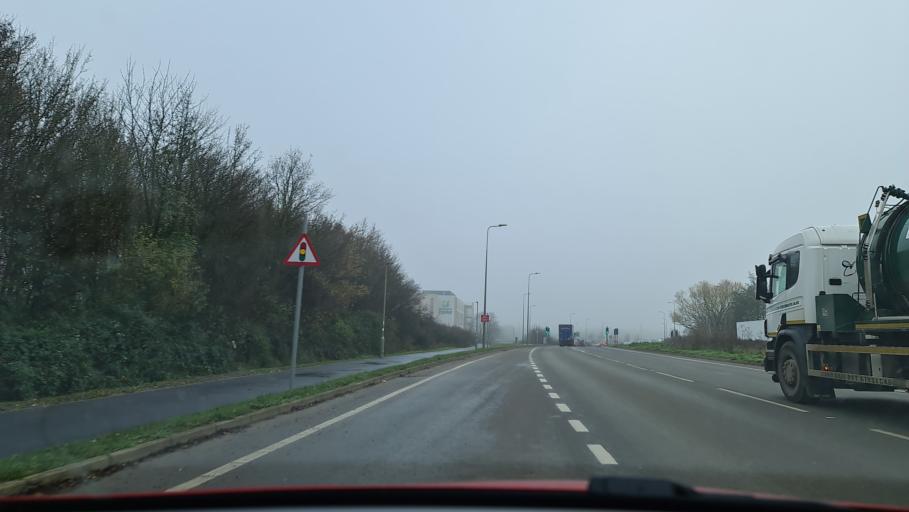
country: GB
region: England
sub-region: Oxfordshire
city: Bicester
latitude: 51.8886
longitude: -1.1660
